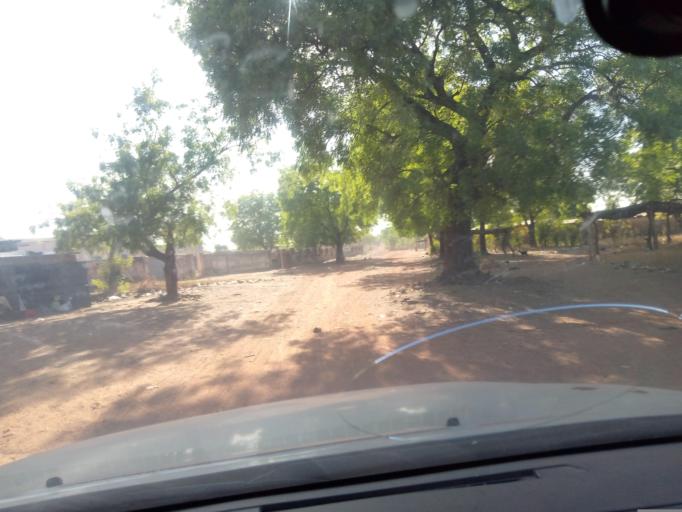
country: ML
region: Sikasso
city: Sikasso
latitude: 11.4860
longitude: -5.4832
